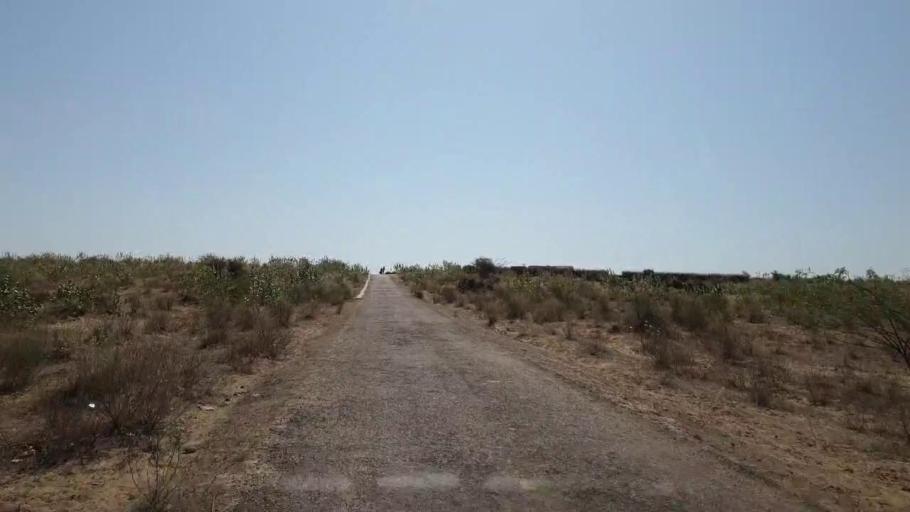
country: PK
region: Sindh
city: Nabisar
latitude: 25.0781
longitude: 69.9817
